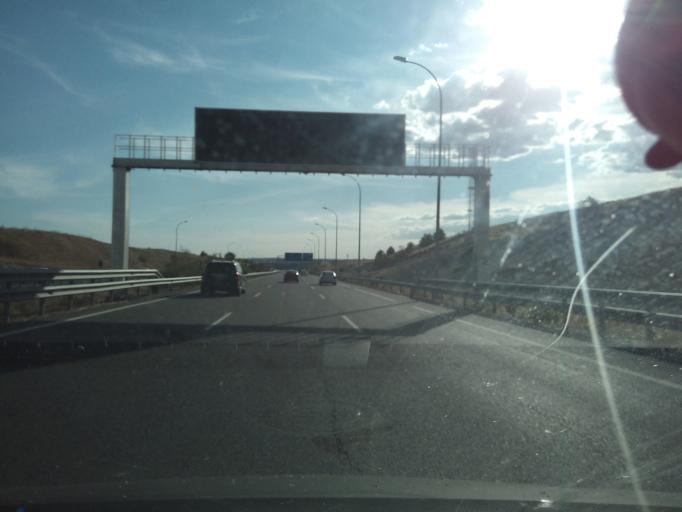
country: ES
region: Madrid
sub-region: Provincia de Madrid
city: Villa de Vallecas
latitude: 40.3390
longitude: -3.6095
